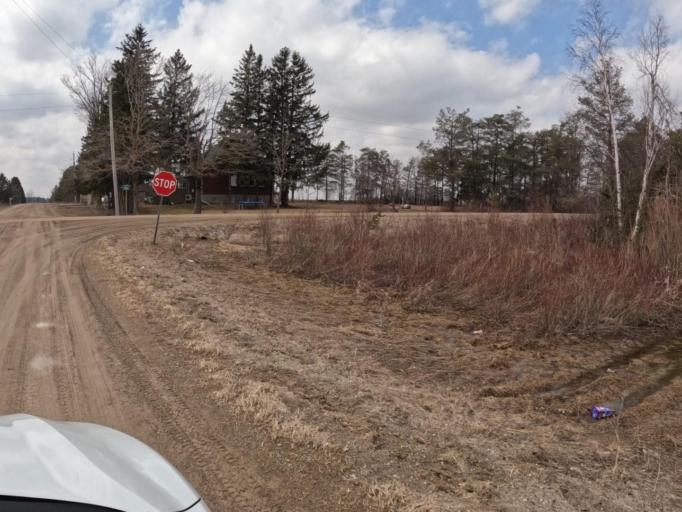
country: CA
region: Ontario
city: Shelburne
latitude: 44.0277
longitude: -80.2627
